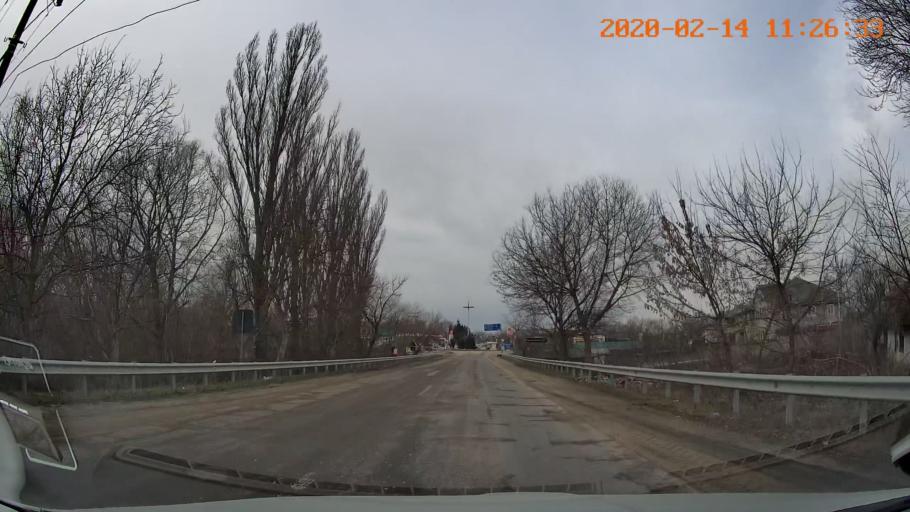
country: MD
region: Briceni
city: Briceni
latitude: 48.3509
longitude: 27.0867
